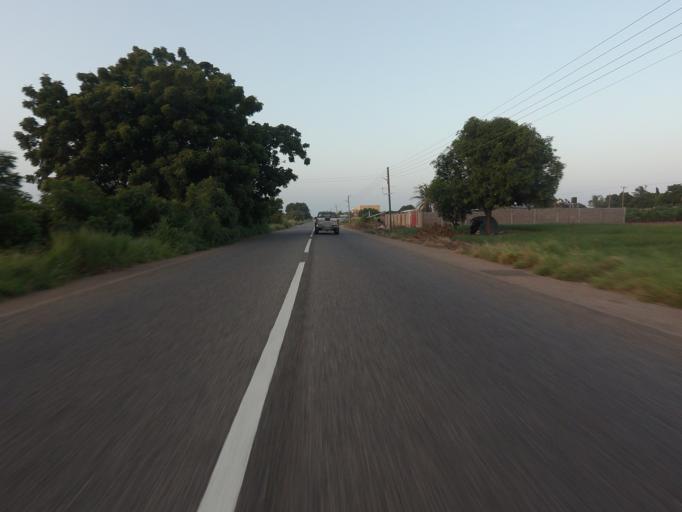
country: GH
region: Volta
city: Anloga
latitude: 5.8170
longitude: 0.9407
